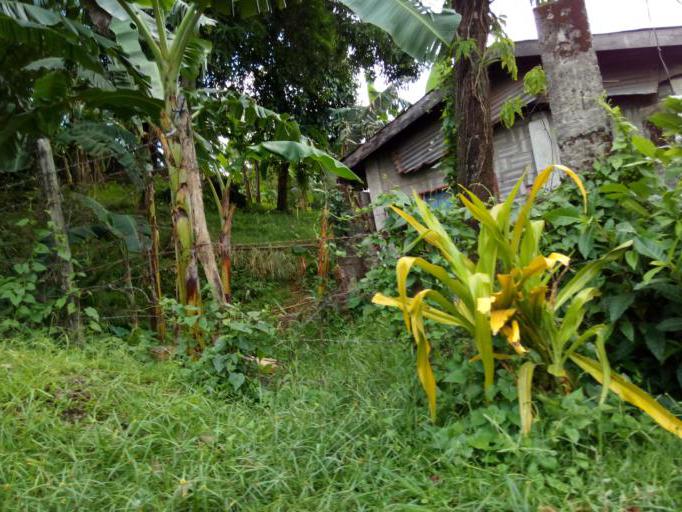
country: PH
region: Caraga
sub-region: Province of Surigao del Norte
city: Surigao
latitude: 9.7796
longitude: 125.4843
